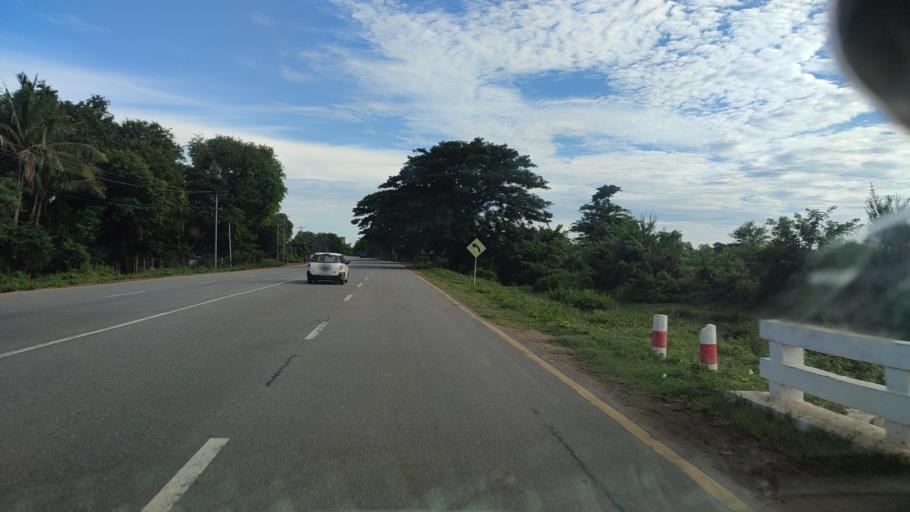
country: MM
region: Mandalay
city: Yamethin
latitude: 20.2070
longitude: 96.1807
